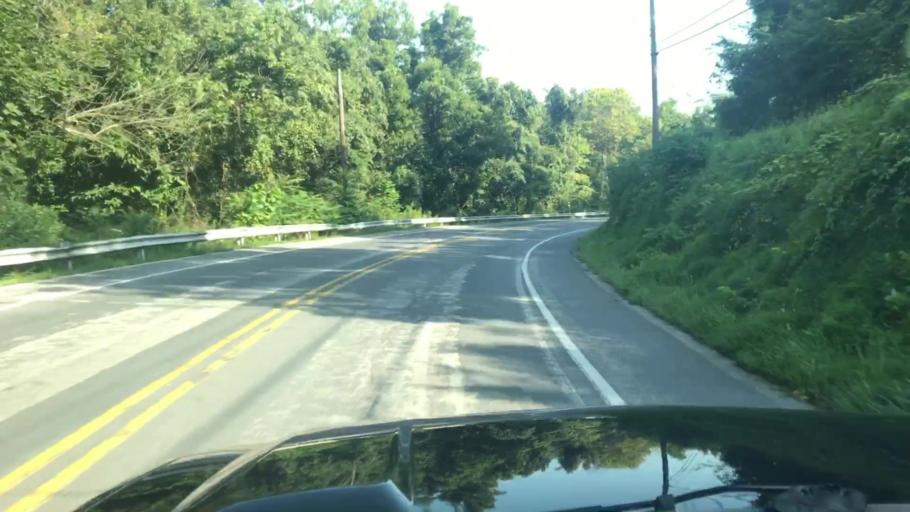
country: US
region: Pennsylvania
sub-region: York County
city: Valley Green
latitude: 40.1632
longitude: -76.8180
